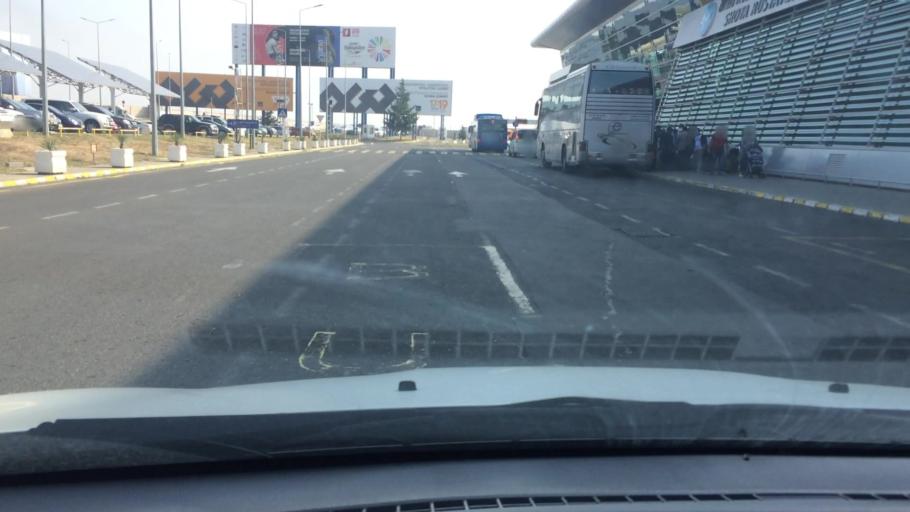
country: GE
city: Didi Lilo
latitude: 41.6701
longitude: 44.9648
